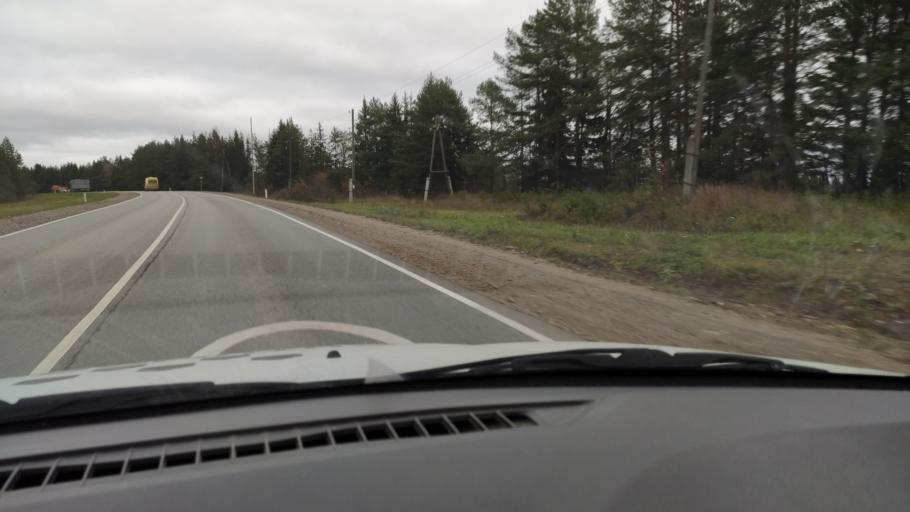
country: RU
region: Kirov
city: Slobodskoy
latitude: 58.7331
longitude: 50.2841
